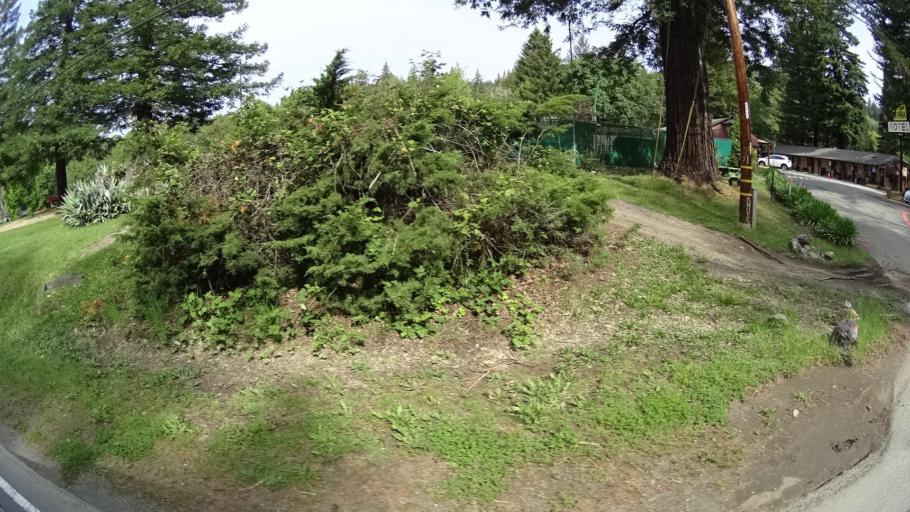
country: US
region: California
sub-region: Humboldt County
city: Redway
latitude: 40.1405
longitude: -123.8103
